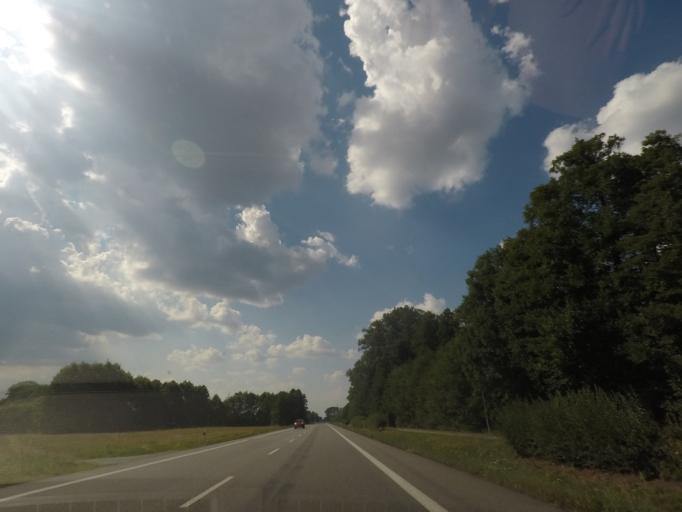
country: CZ
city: Tyniste nad Orlici
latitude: 50.1605
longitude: 16.0584
